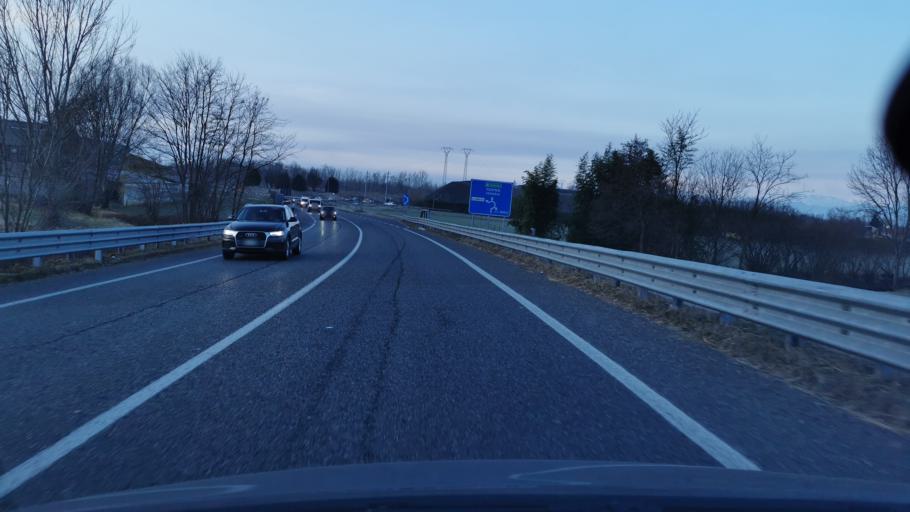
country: IT
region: Piedmont
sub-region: Provincia di Torino
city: Borgaro Torinese
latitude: 45.1559
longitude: 7.6451
